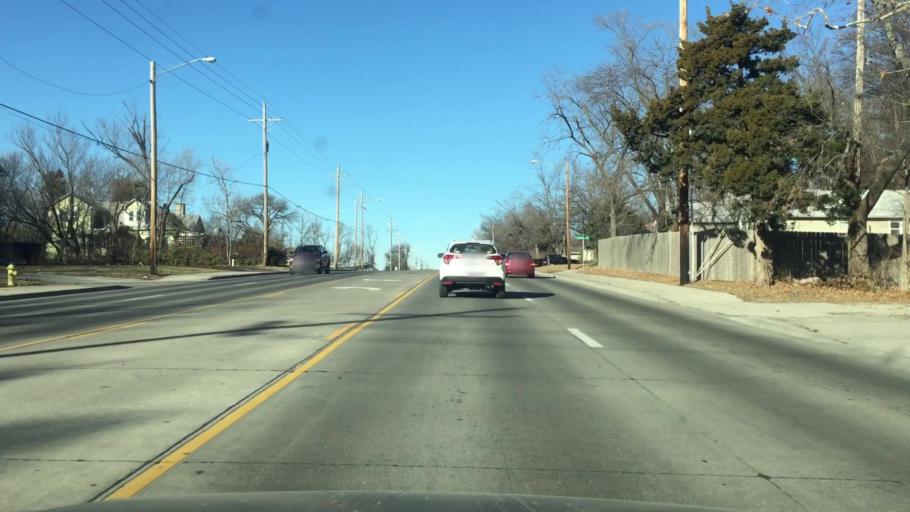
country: US
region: Kansas
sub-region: Douglas County
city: Lawrence
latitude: 38.9609
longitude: -95.2604
